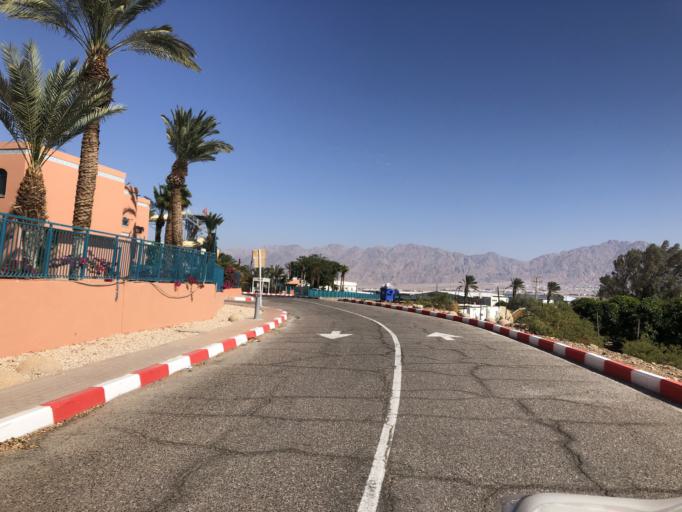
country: IL
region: Southern District
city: Eilat
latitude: 29.5792
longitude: 34.9628
